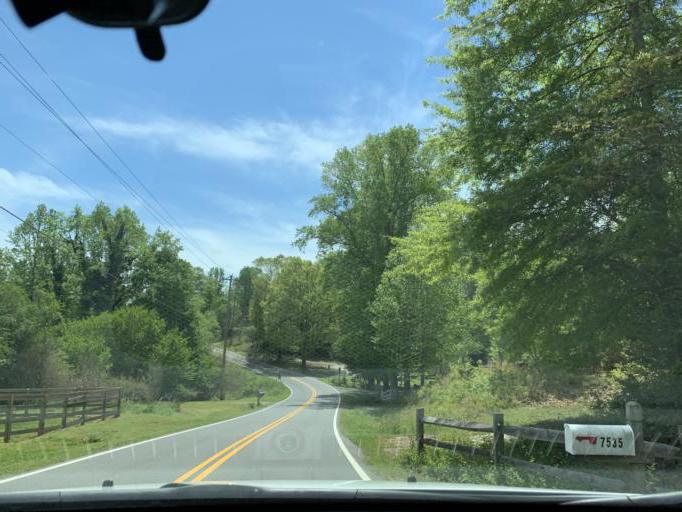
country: US
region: Georgia
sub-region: Hall County
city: Flowery Branch
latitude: 34.2642
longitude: -84.0222
